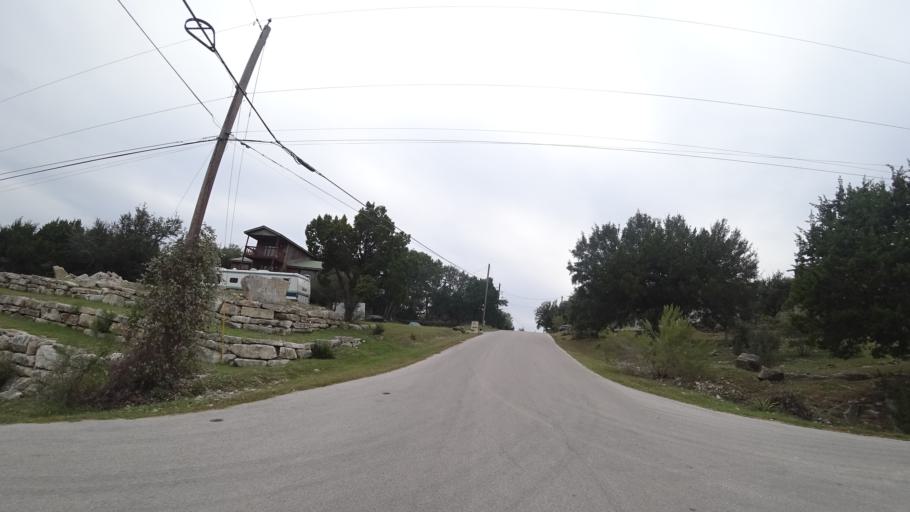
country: US
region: Texas
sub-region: Travis County
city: Hudson Bend
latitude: 30.3695
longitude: -97.9189
